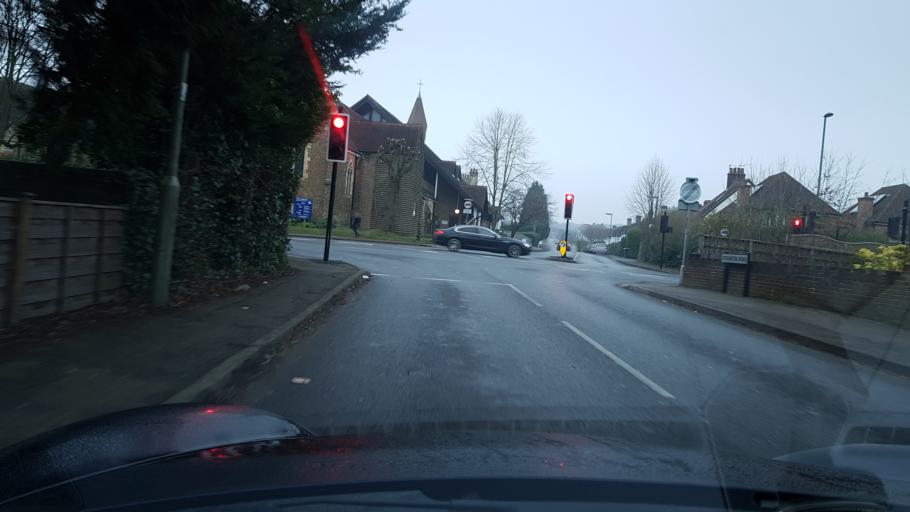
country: GB
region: England
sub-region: Surrey
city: Guildford
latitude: 51.2552
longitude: -0.5932
